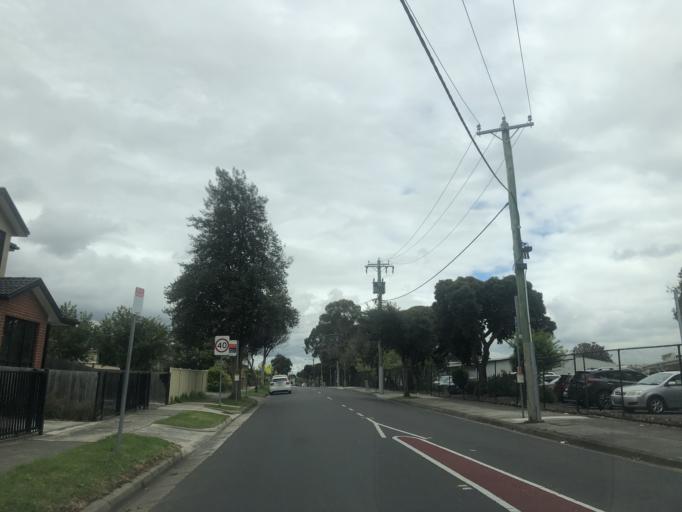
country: AU
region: Victoria
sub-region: Greater Dandenong
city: Dandenong North
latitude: -37.9657
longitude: 145.2056
